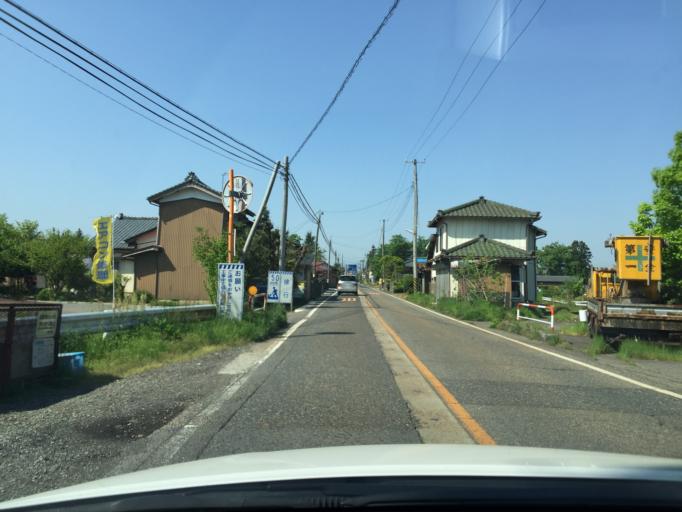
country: JP
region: Niigata
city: Muramatsu
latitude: 37.7019
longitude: 139.1928
